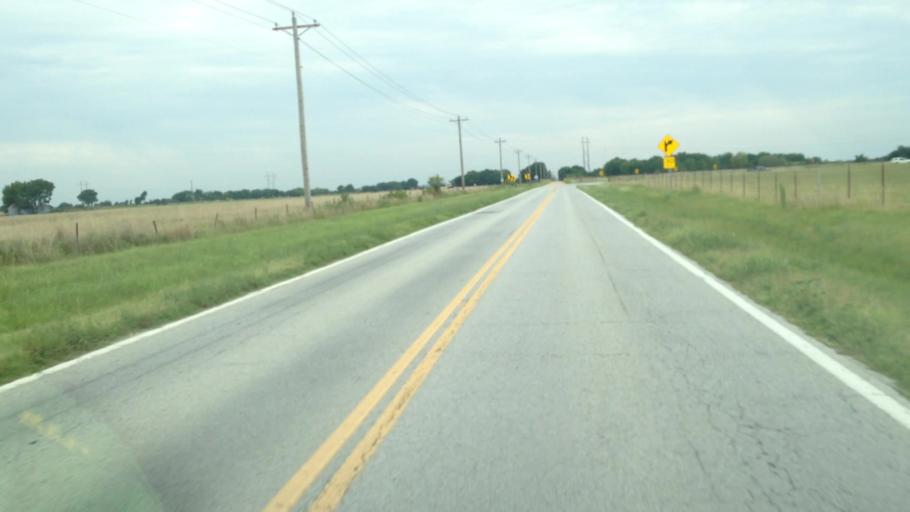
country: US
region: Oklahoma
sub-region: Delaware County
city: Cleora
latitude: 36.6126
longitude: -94.9787
